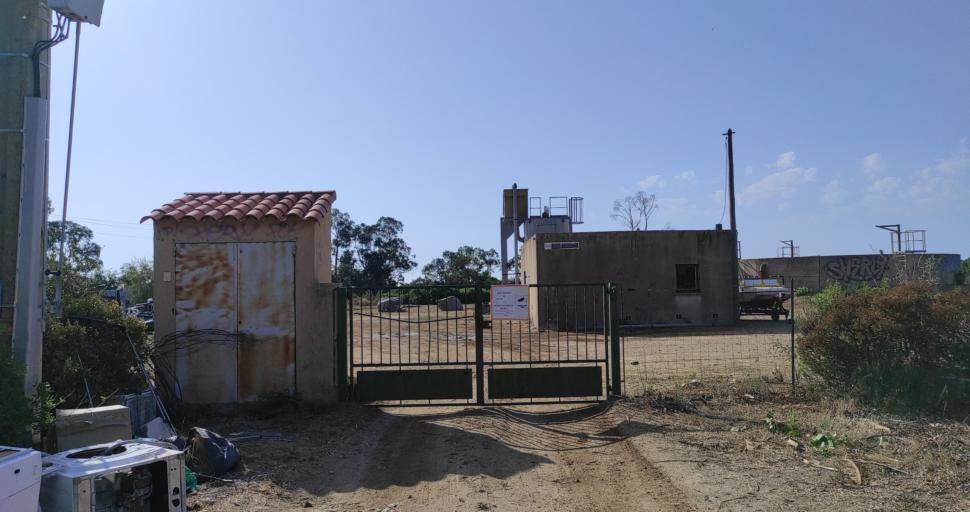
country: FR
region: Corsica
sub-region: Departement de la Corse-du-Sud
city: Porto-Vecchio
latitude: 41.6441
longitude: 9.3434
